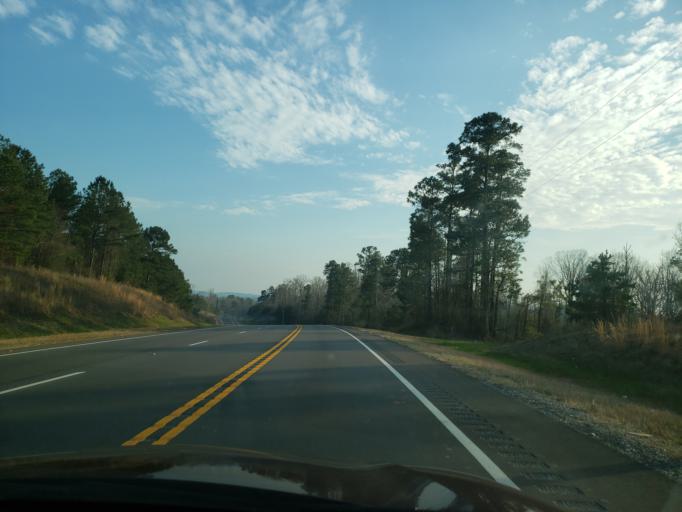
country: US
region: Alabama
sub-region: Hale County
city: Moundville
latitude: 32.8662
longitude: -87.6131
